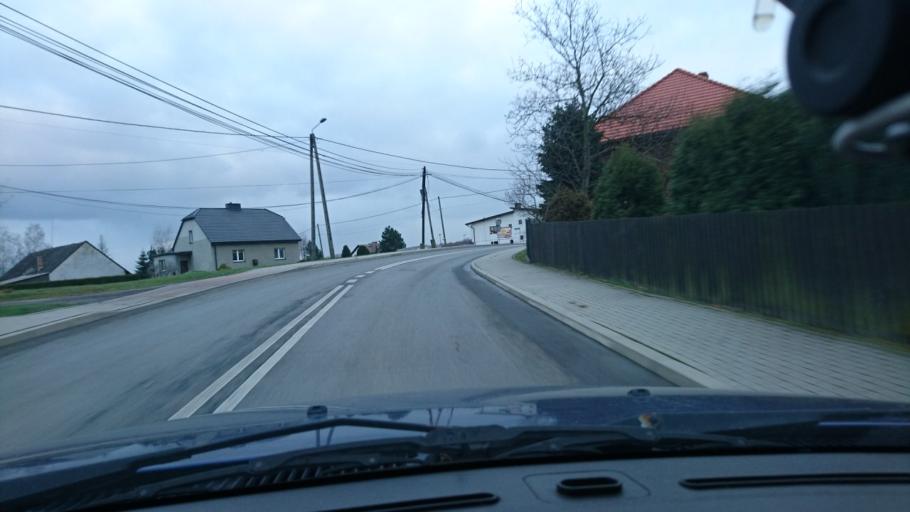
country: PL
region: Silesian Voivodeship
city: Janowice
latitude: 49.8878
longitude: 19.0903
